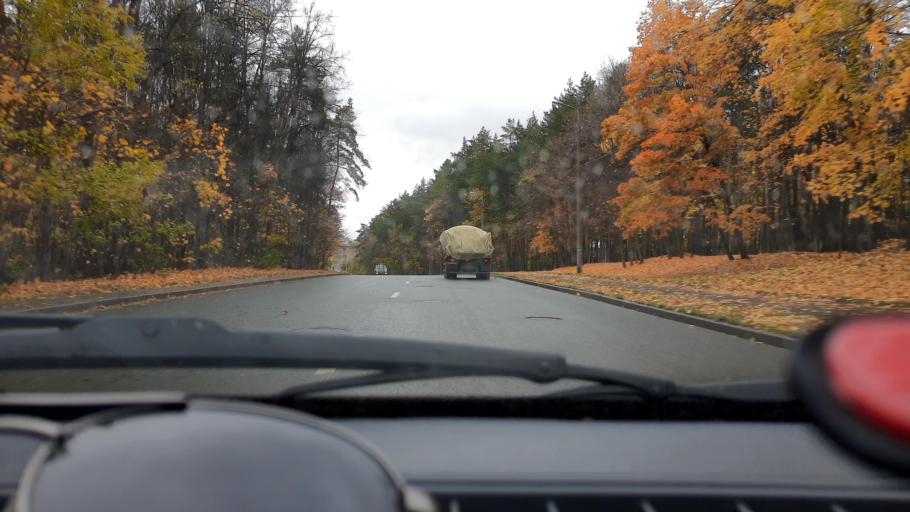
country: RU
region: Bashkortostan
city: Ufa
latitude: 54.7839
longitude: 56.0272
